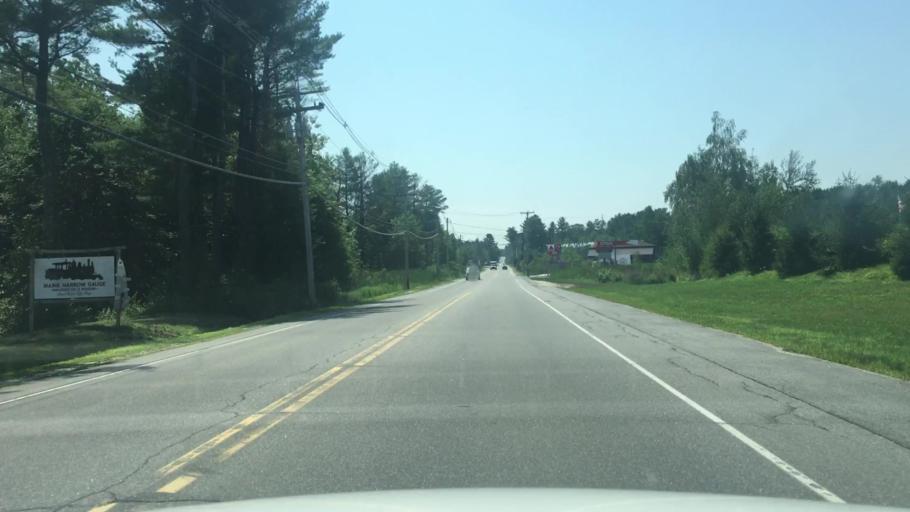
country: US
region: Maine
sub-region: Cumberland County
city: New Gloucester
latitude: 43.8802
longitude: -70.3291
